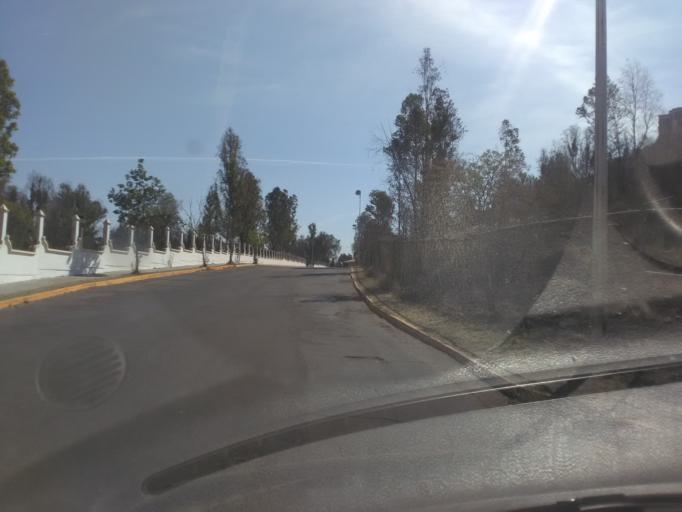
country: MX
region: Durango
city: Victoria de Durango
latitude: 24.0237
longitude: -104.6854
